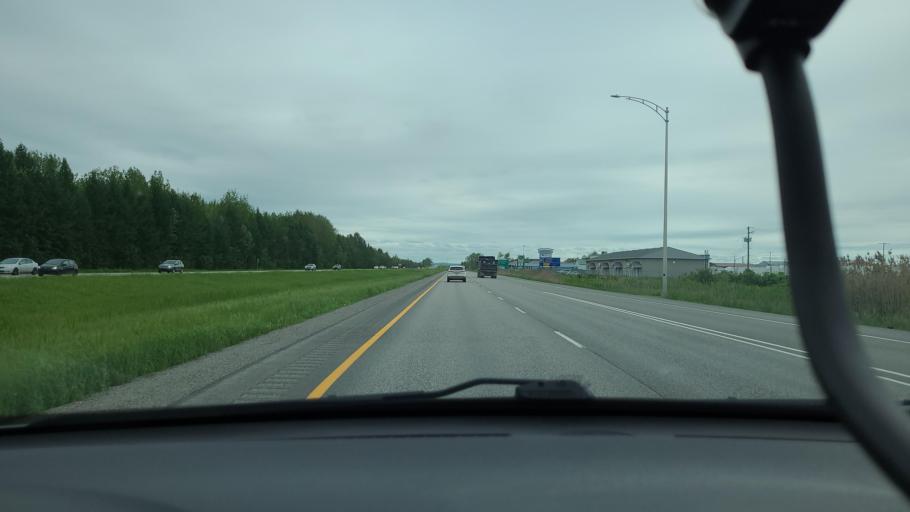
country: CA
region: Quebec
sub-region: Lanaudiere
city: Mascouche
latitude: 45.8254
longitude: -73.6078
